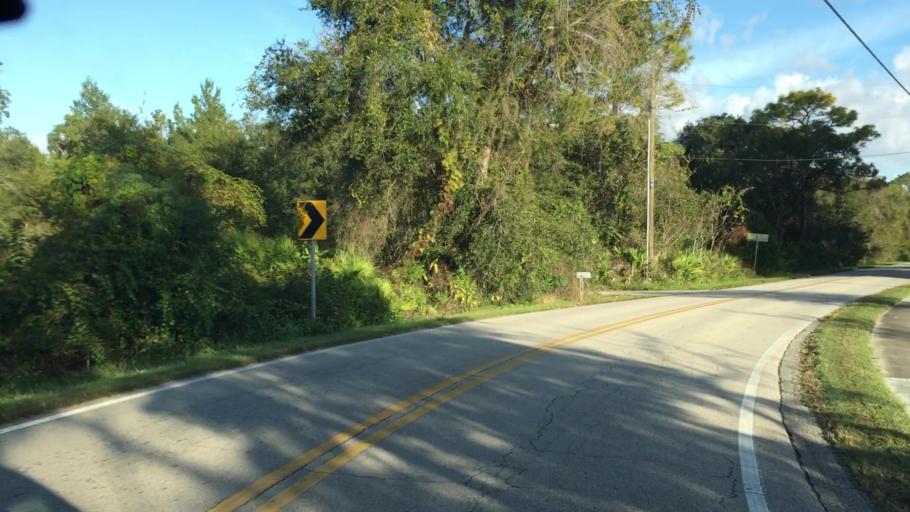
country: US
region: Florida
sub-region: Volusia County
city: North DeLand
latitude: 29.0664
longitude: -81.2713
